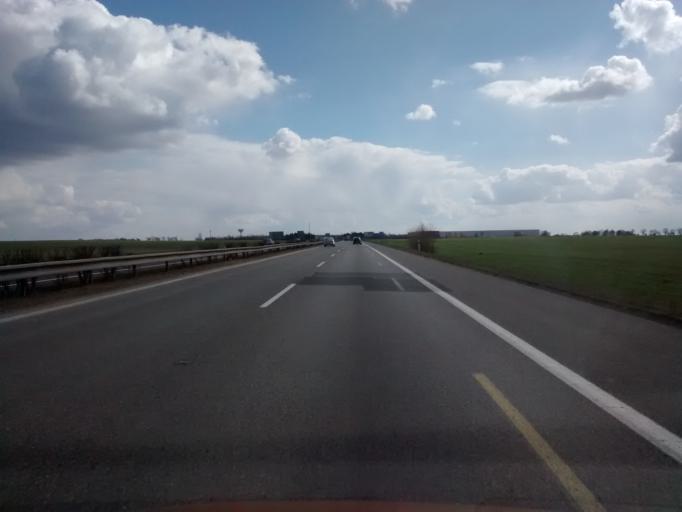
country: CZ
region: Central Bohemia
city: Zdiby
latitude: 50.1934
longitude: 14.4421
